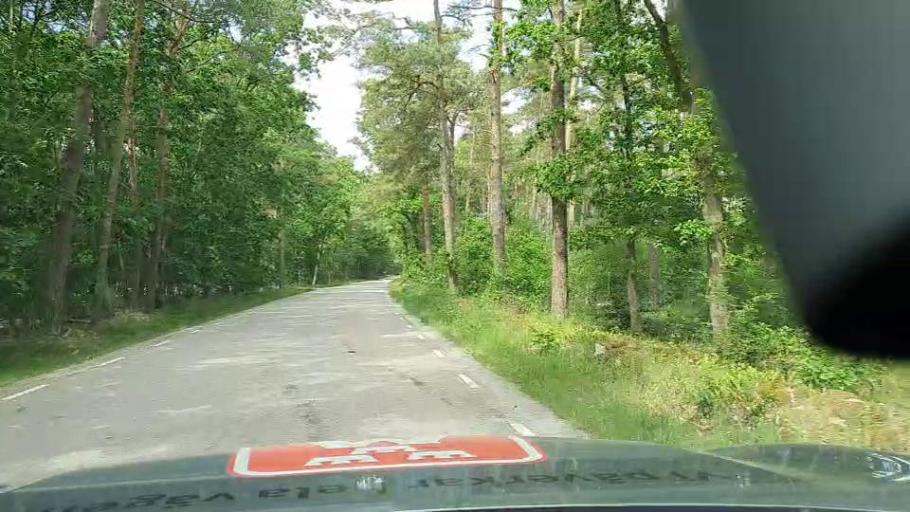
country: SE
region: Blekinge
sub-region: Karlshamns Kommun
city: Morrum
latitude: 56.0985
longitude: 14.6880
